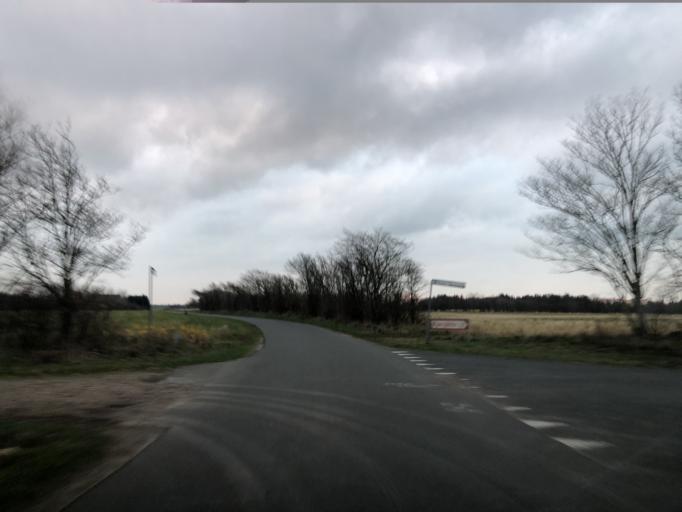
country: DK
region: Central Jutland
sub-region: Holstebro Kommune
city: Ulfborg
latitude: 56.2413
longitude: 8.2868
